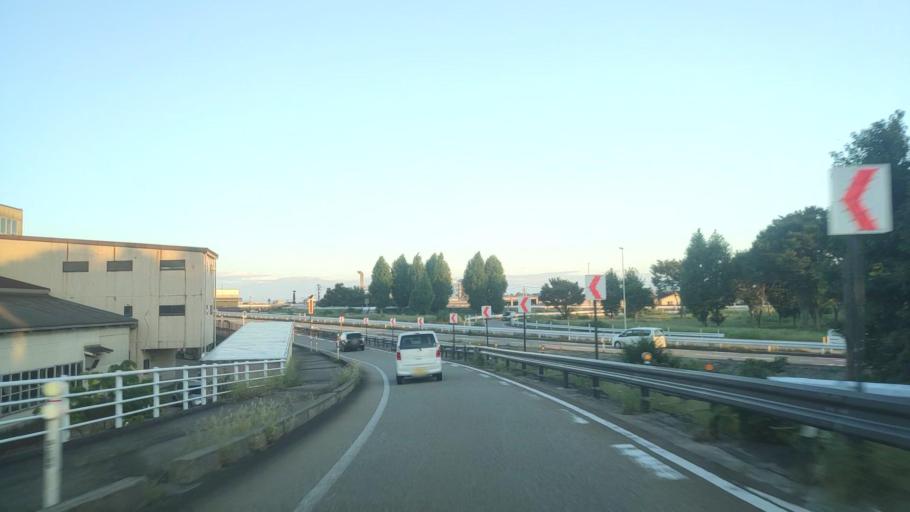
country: JP
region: Toyama
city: Takaoka
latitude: 36.7624
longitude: 137.0072
